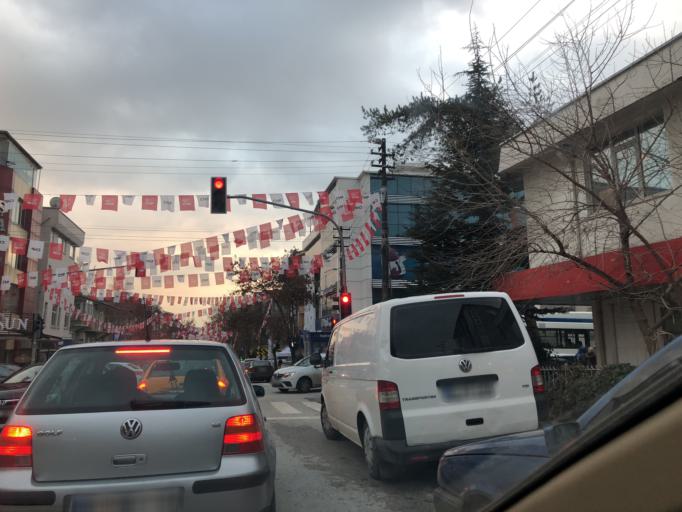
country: TR
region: Ankara
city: Ankara
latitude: 39.9665
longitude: 32.8085
